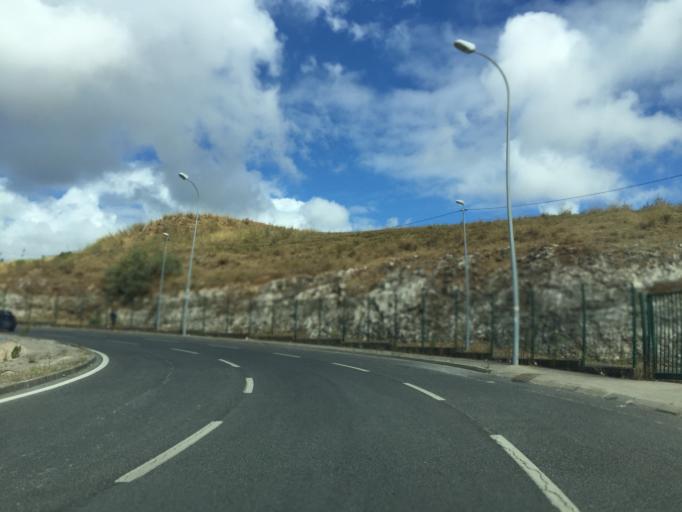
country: PT
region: Lisbon
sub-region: Amadora
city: Amadora
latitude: 38.7717
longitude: -9.2249
